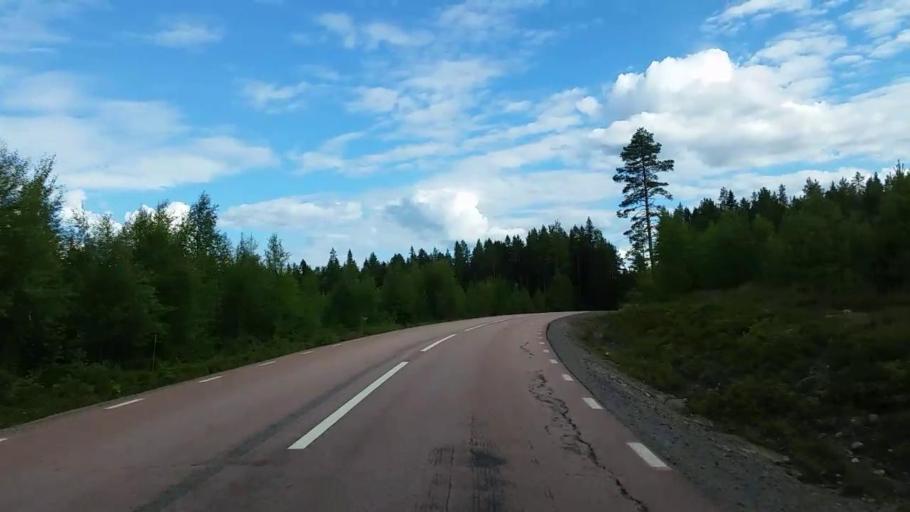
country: SE
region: Gaevleborg
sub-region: Ljusdals Kommun
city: Farila
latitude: 61.9879
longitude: 15.8544
